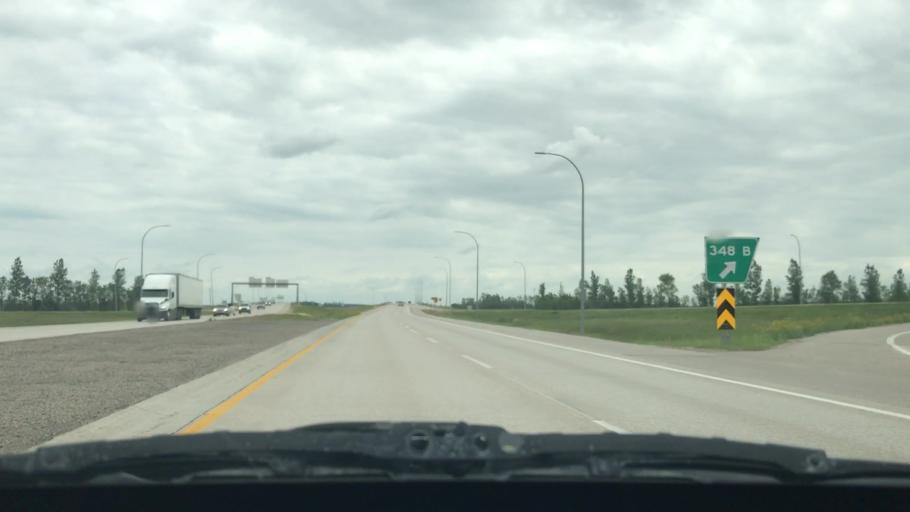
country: CA
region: Manitoba
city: Winnipeg
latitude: 49.8339
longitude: -96.9620
